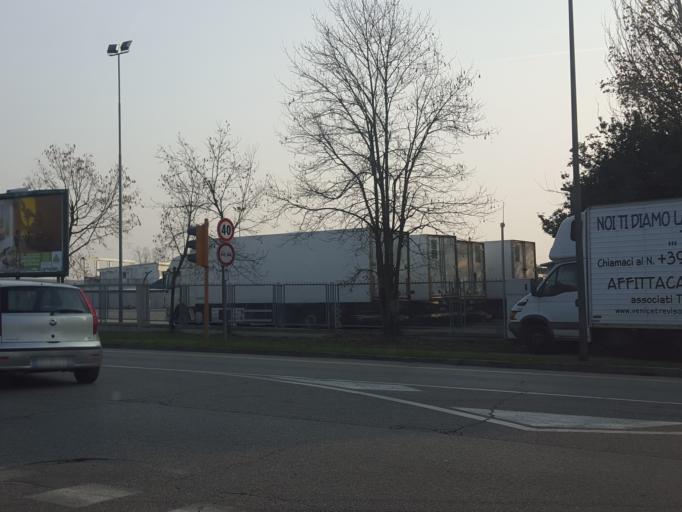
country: IT
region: Veneto
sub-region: Provincia di Treviso
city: Treviso
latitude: 45.6688
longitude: 12.2186
